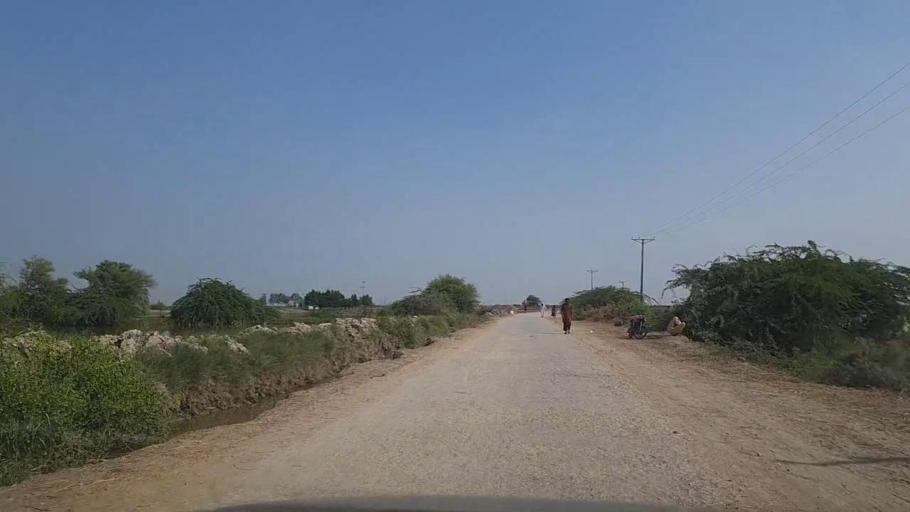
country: PK
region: Sindh
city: Thatta
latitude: 24.5844
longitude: 67.9060
